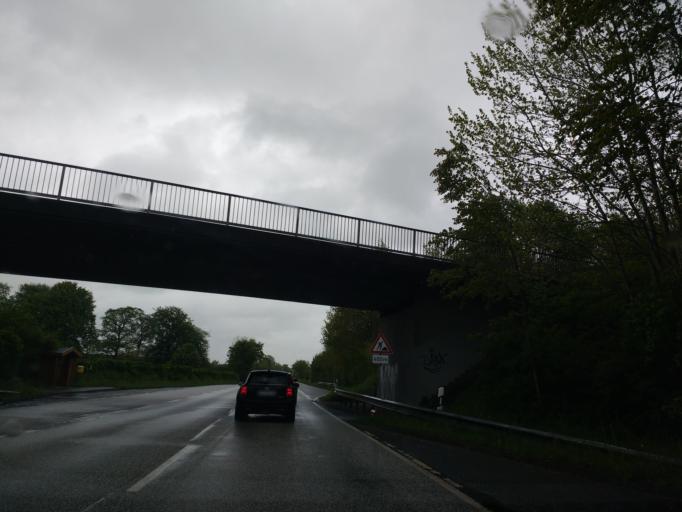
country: DE
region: Schleswig-Holstein
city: Barkelsby
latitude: 54.4995
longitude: 9.8474
